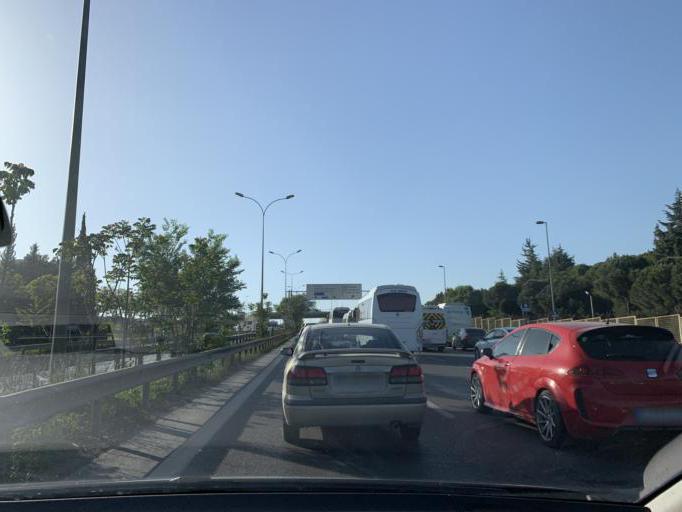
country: TR
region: Kocaeli
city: Darica
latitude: 40.8195
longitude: 29.3586
